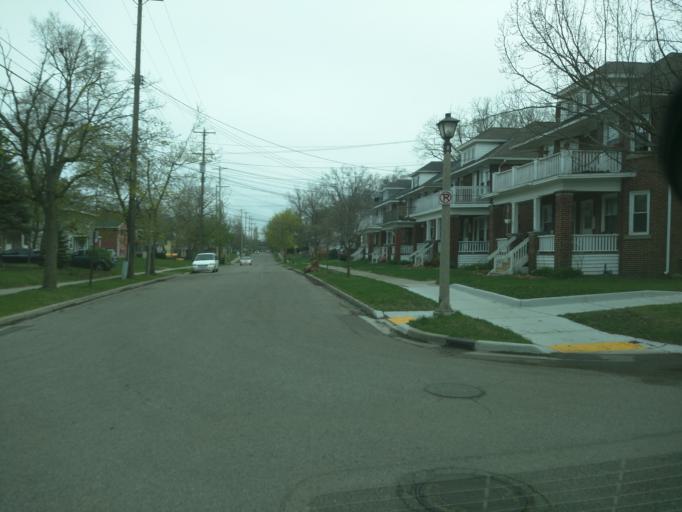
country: US
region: Michigan
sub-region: Ingham County
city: Lansing
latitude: 42.7311
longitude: -84.5330
